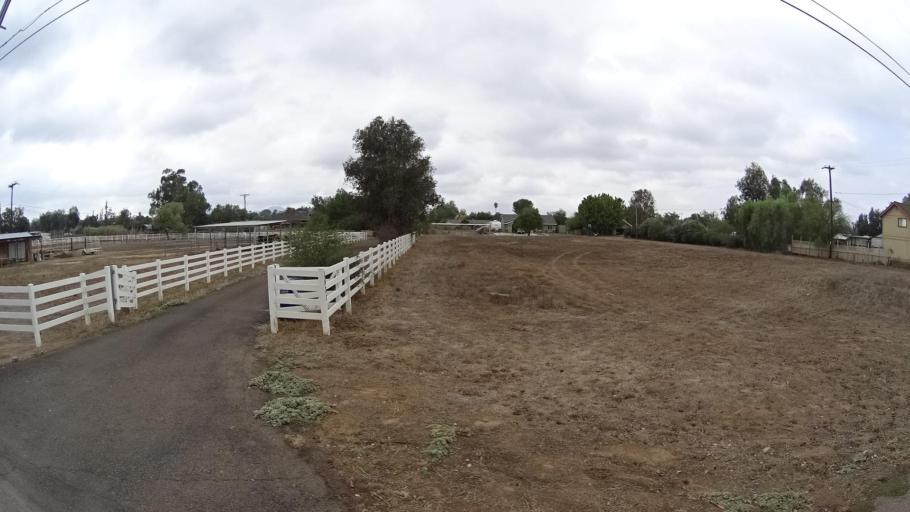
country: US
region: California
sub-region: San Diego County
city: Ramona
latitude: 33.0239
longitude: -116.8621
